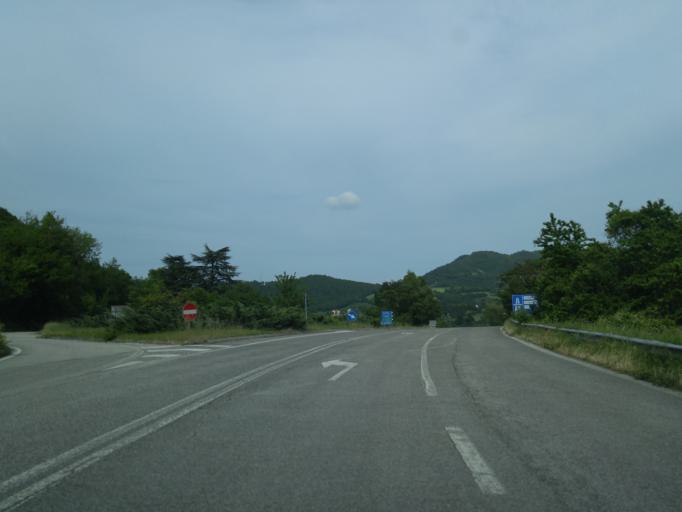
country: IT
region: The Marches
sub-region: Provincia di Pesaro e Urbino
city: Canavaccio
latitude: 43.6647
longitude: 12.7514
